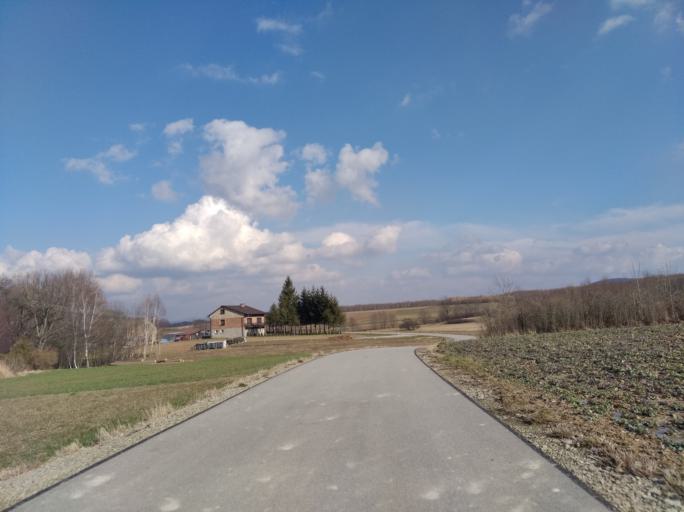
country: PL
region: Subcarpathian Voivodeship
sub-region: Powiat strzyzowski
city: Wysoka Strzyzowska
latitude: 49.8470
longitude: 21.7062
